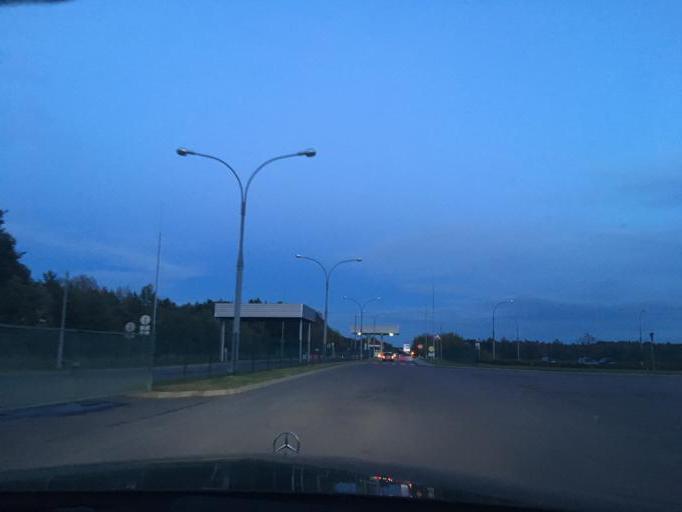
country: PL
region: Lublin Voivodeship
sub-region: Powiat bialski
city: Slawatycze
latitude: 51.7630
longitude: 23.6020
